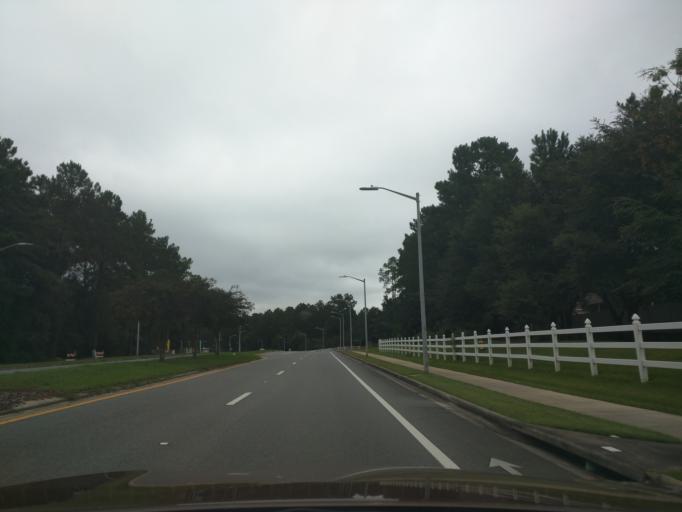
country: US
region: Florida
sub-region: Leon County
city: Tallahassee
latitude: 30.4368
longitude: -84.2017
